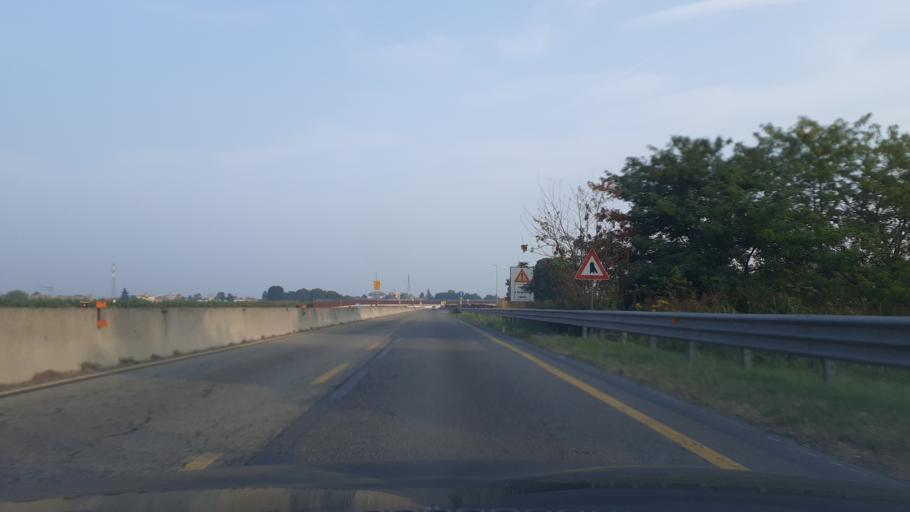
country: IT
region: Lombardy
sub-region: Citta metropolitana di Milano
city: Cormano
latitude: 45.5508
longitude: 9.1468
